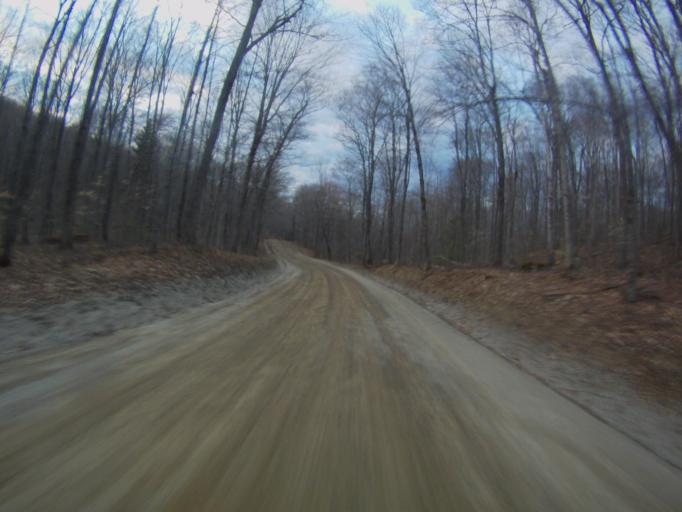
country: US
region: Vermont
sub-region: Rutland County
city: Brandon
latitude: 43.9331
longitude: -73.0201
